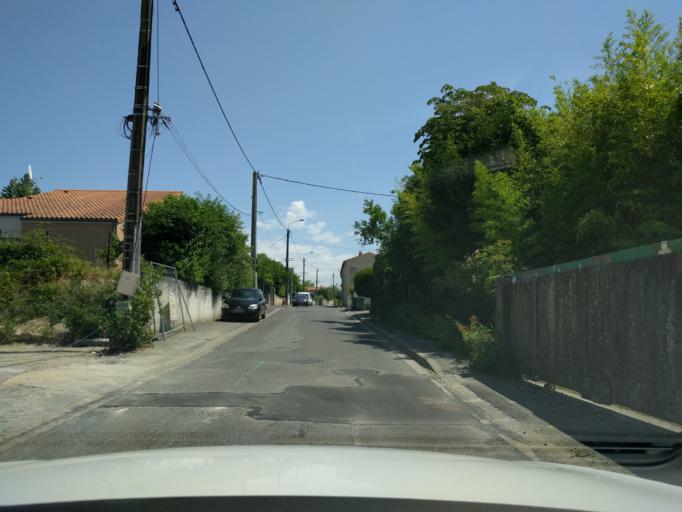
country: FR
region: Poitou-Charentes
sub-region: Departement des Deux-Sevres
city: Niort
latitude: 46.3482
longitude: -0.4754
